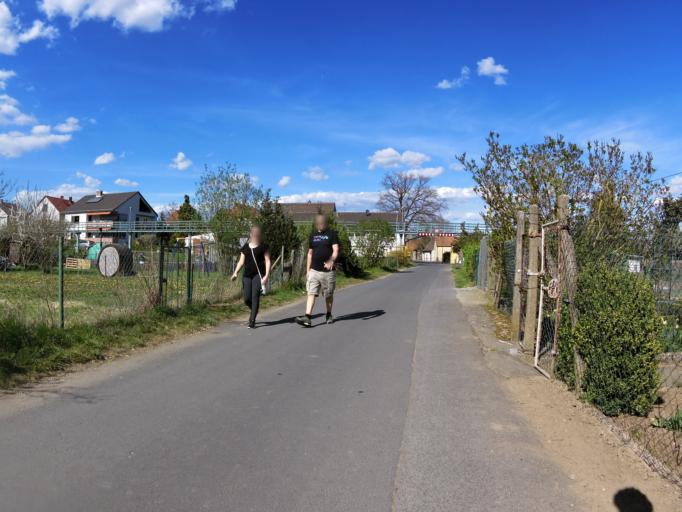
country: DE
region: Bavaria
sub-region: Regierungsbezirk Unterfranken
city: Volkach
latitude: 49.8602
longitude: 10.2170
